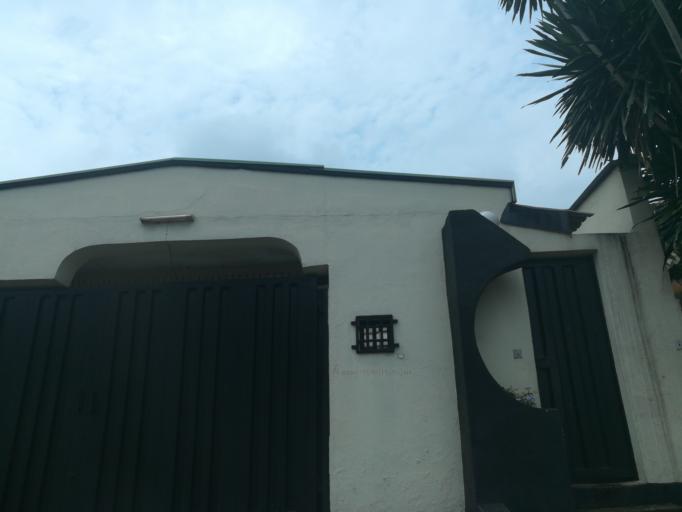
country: NG
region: Lagos
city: Ojota
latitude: 6.5890
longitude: 3.3667
